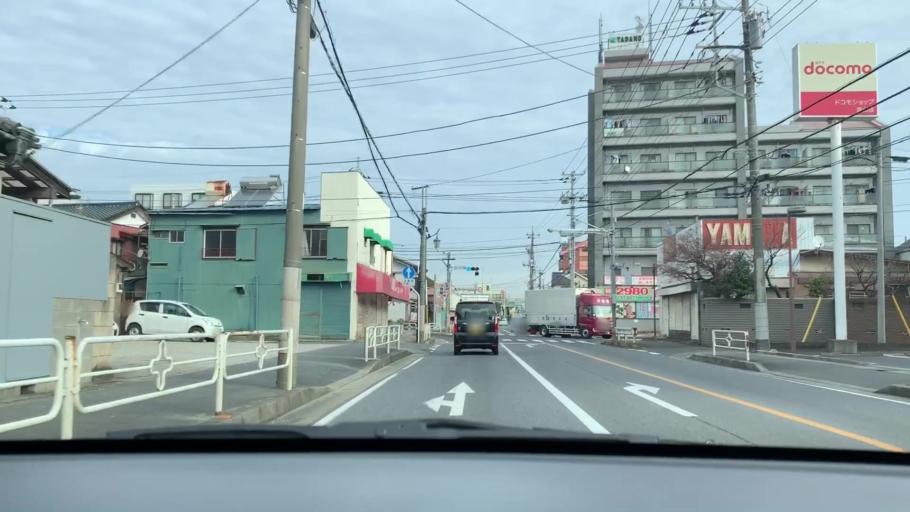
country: JP
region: Chiba
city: Nagareyama
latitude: 35.8512
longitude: 139.8987
